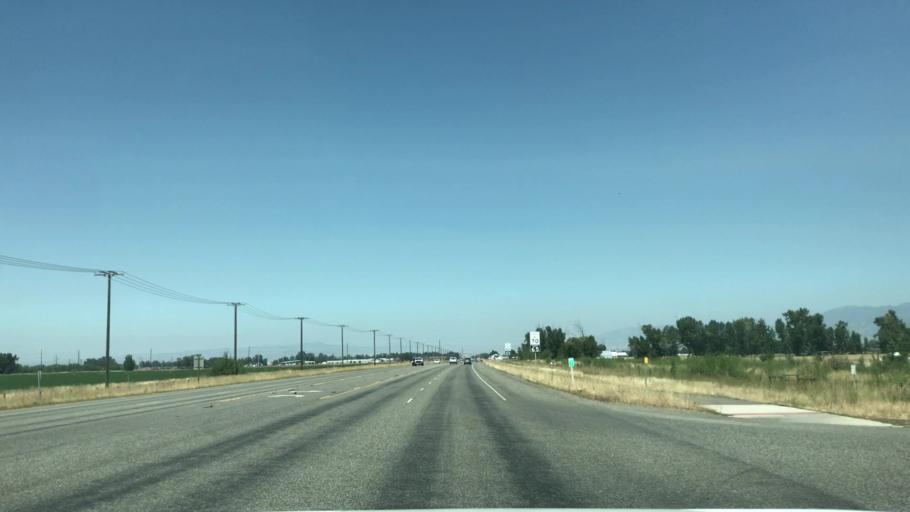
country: US
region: Montana
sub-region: Gallatin County
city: Four Corners
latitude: 45.6853
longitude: -111.1858
